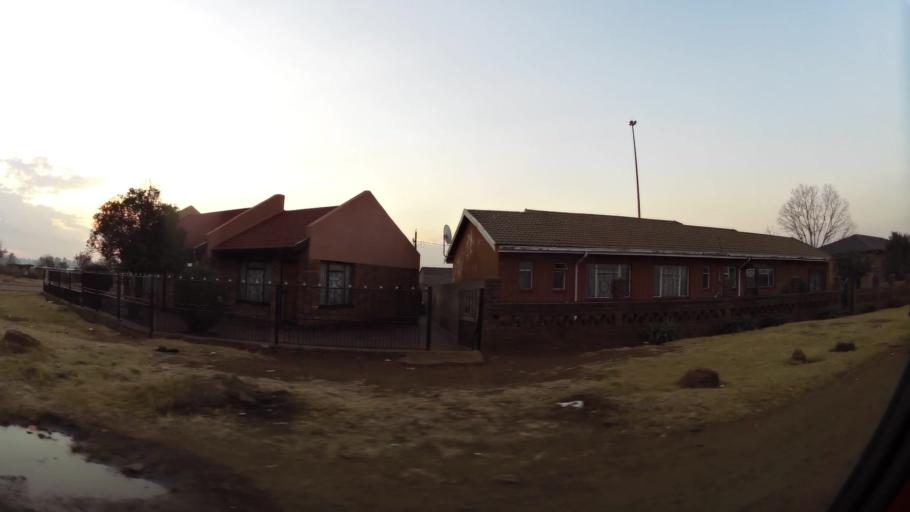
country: ZA
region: Gauteng
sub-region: City of Johannesburg Metropolitan Municipality
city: Orange Farm
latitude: -26.5466
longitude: 27.8746
